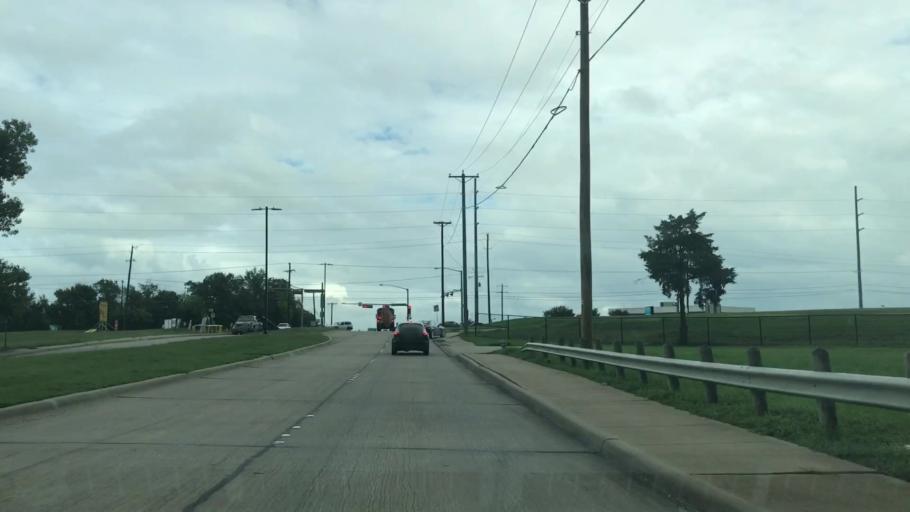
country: US
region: Texas
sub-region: Dallas County
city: Garland
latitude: 32.8878
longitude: -96.6125
